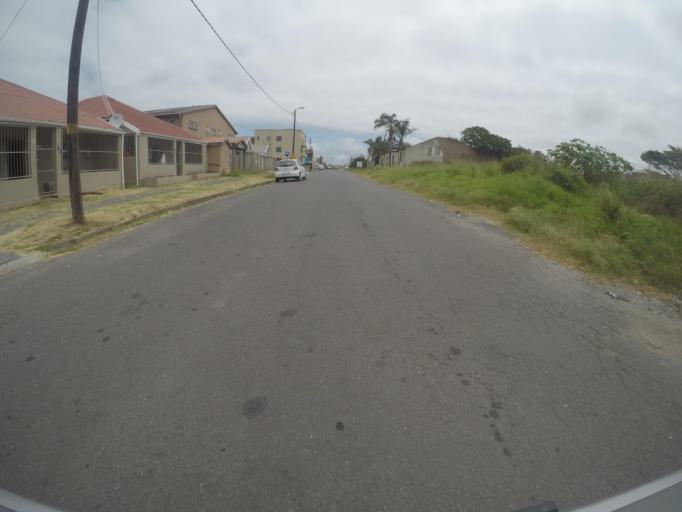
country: ZA
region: Eastern Cape
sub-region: Buffalo City Metropolitan Municipality
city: East London
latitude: -33.0129
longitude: 27.9128
